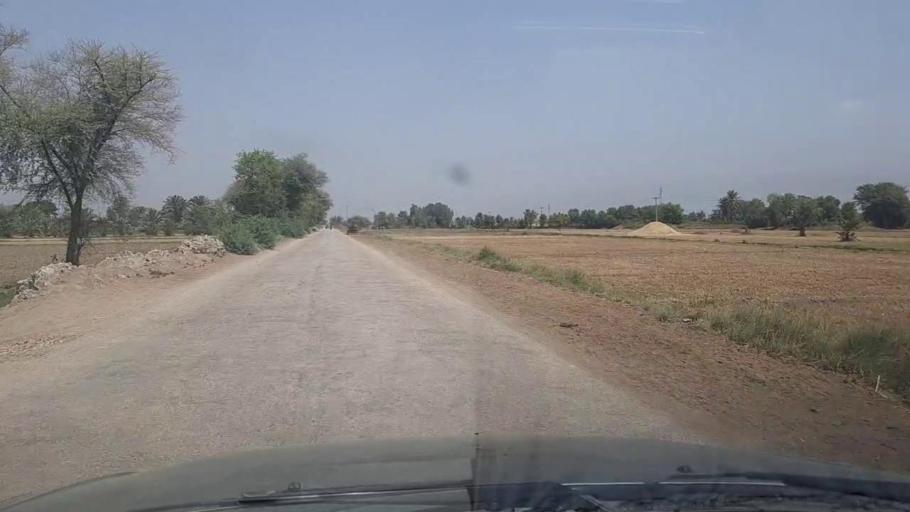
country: PK
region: Sindh
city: Setharja Old
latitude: 27.1420
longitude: 68.5271
